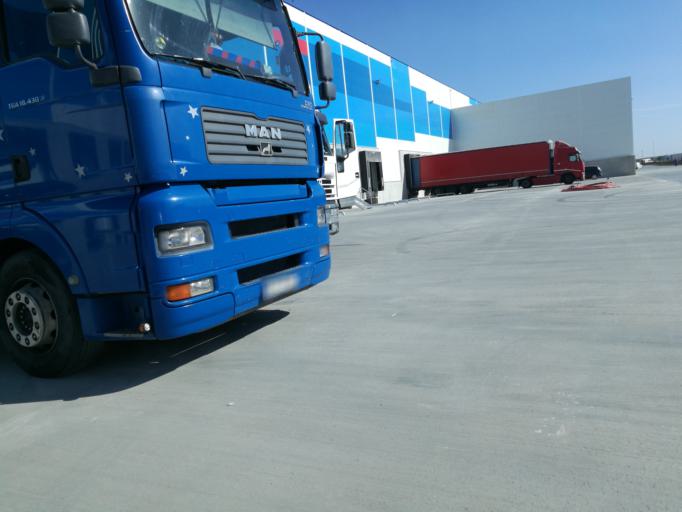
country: RO
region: Giurgiu
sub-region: Comuna Joita
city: Bacu
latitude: 44.4673
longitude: 25.8746
